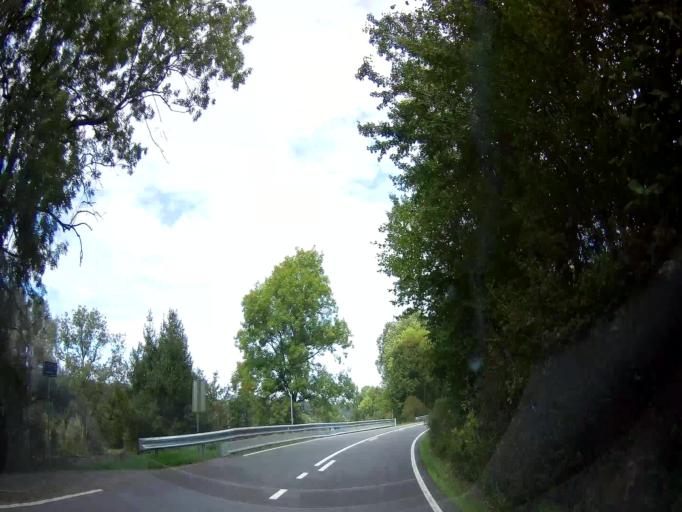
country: BE
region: Wallonia
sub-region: Province du Luxembourg
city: Durbuy
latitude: 50.3573
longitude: 5.5086
